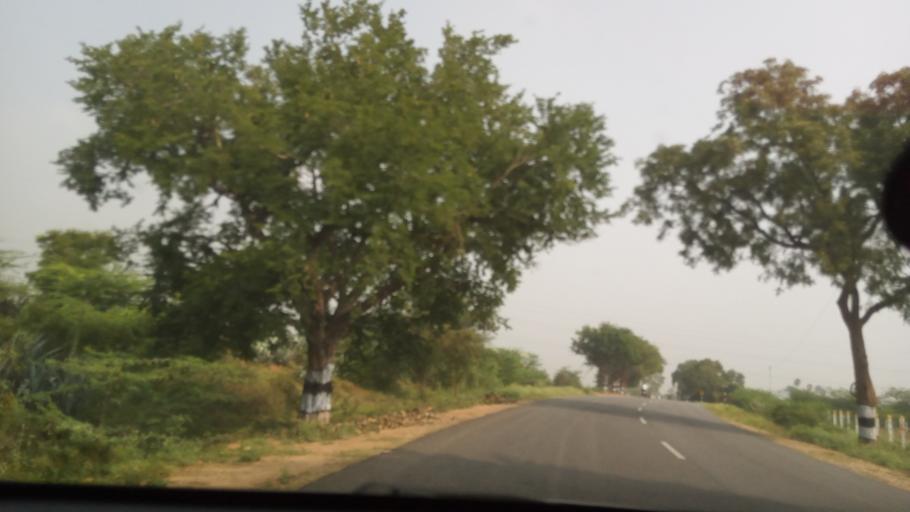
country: IN
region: Tamil Nadu
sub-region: Erode
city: Punjai Puliyampatti
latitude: 11.3916
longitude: 77.1779
